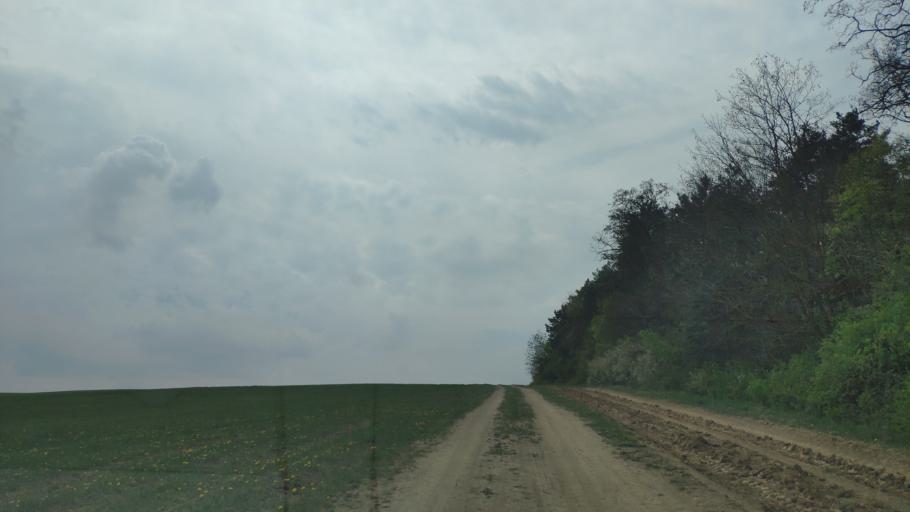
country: SK
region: Kosicky
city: Moldava nad Bodvou
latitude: 48.5609
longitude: 20.9444
